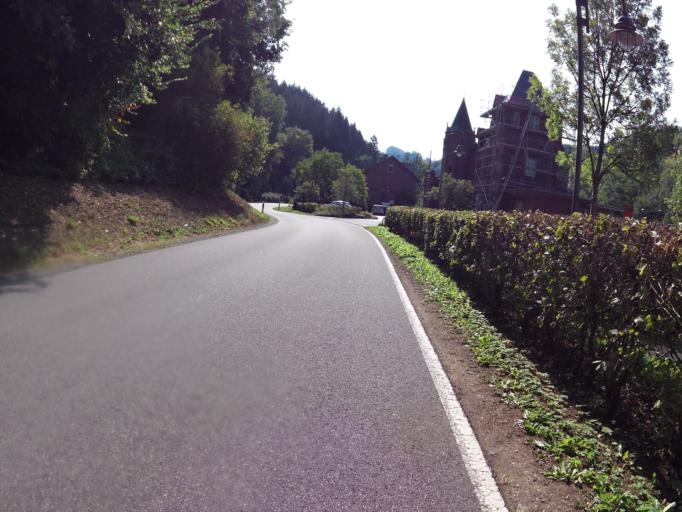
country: DE
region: Rheinland-Pfalz
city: Speicher
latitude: 49.9296
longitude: 6.6157
